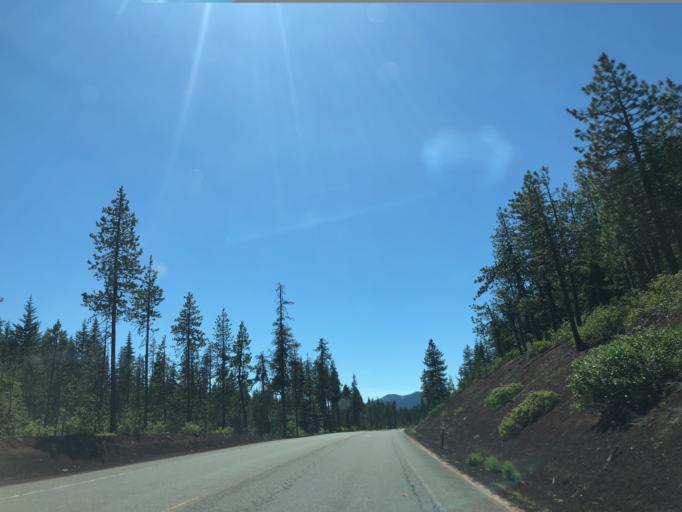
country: US
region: Oregon
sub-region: Deschutes County
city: Sisters
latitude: 44.4335
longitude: -121.9538
